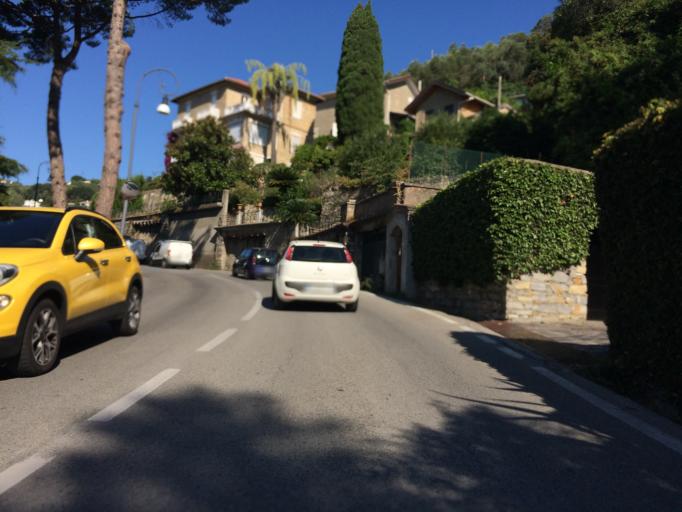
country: IT
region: Liguria
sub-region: Provincia di Genova
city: Rapallo
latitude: 44.3445
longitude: 9.2204
